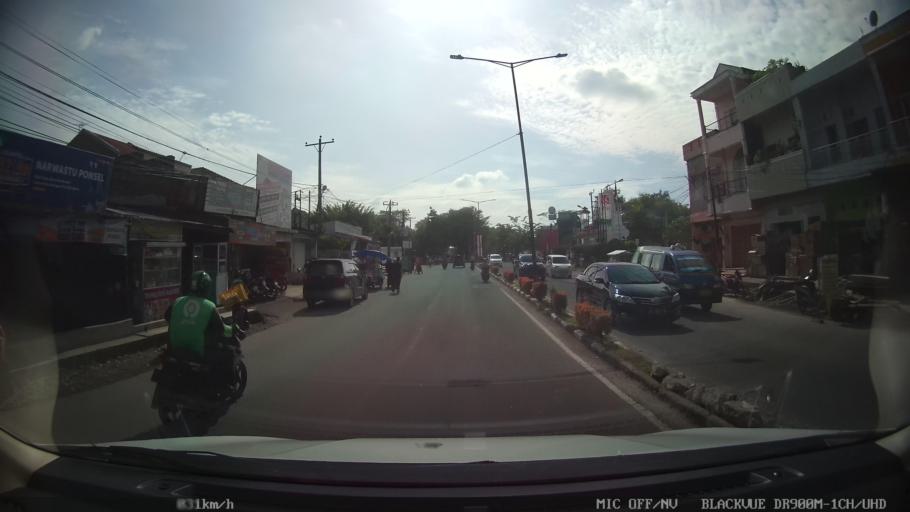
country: ID
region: North Sumatra
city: Medan
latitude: 3.5675
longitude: 98.6521
